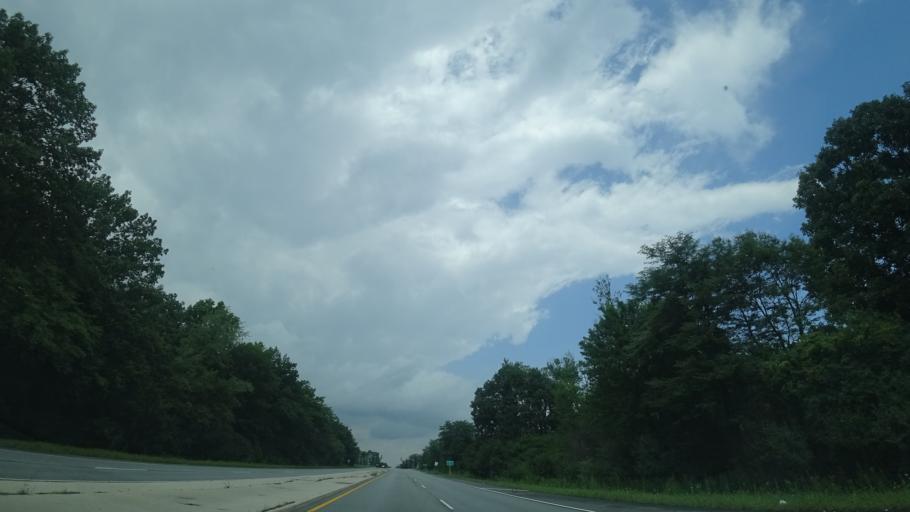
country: US
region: Illinois
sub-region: Cook County
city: Country Club Hills
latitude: 41.5401
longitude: -87.7326
